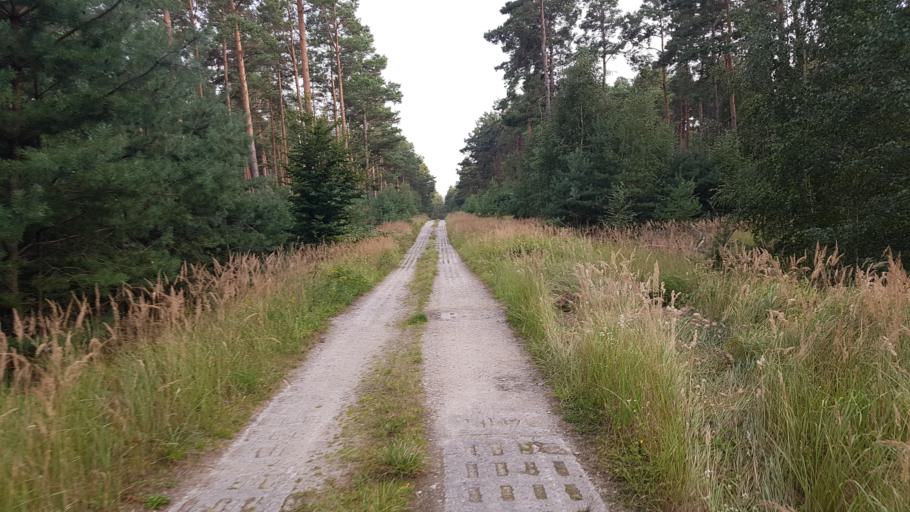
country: DE
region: Brandenburg
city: Schonborn
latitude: 51.6350
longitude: 13.4973
